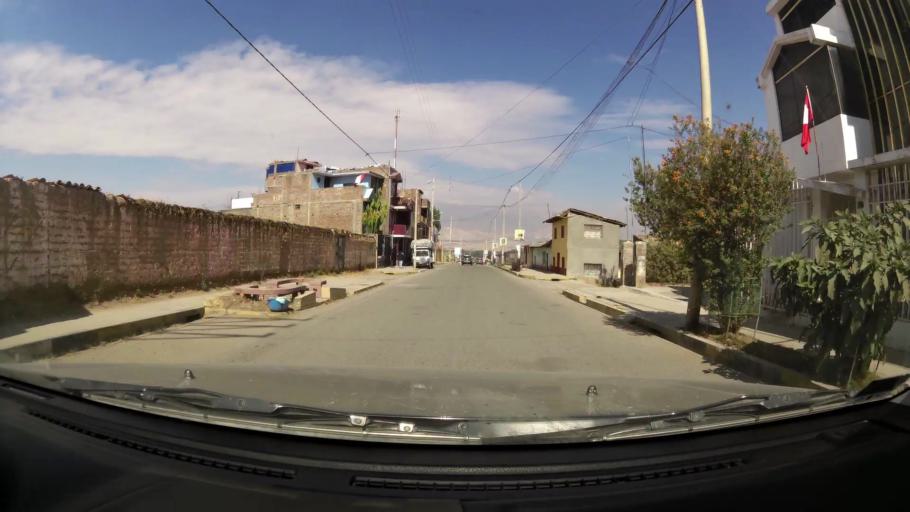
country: PE
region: Junin
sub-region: Provincia de Huancayo
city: El Tambo
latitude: -12.0777
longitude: -75.2248
